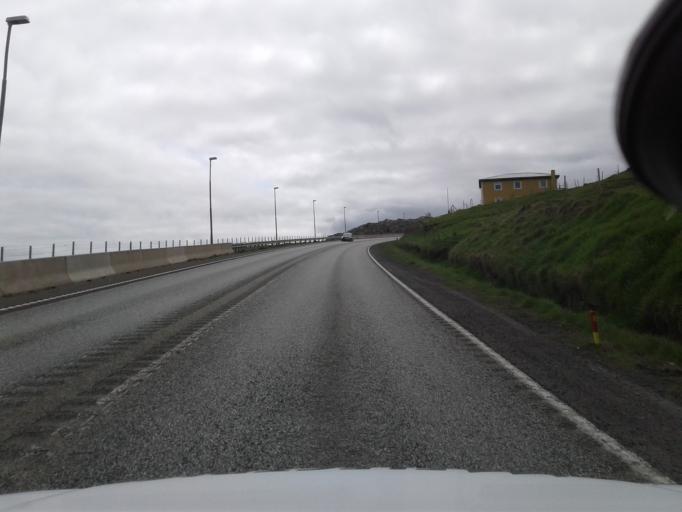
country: FO
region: Streymoy
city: Hoyvik
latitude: 62.0408
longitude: -6.7693
